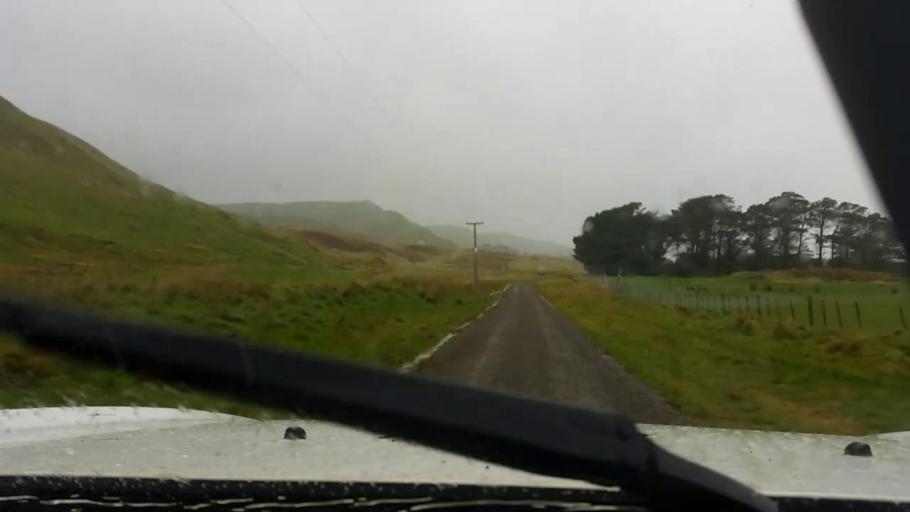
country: NZ
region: Wellington
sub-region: Masterton District
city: Masterton
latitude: -41.2542
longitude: 175.9104
